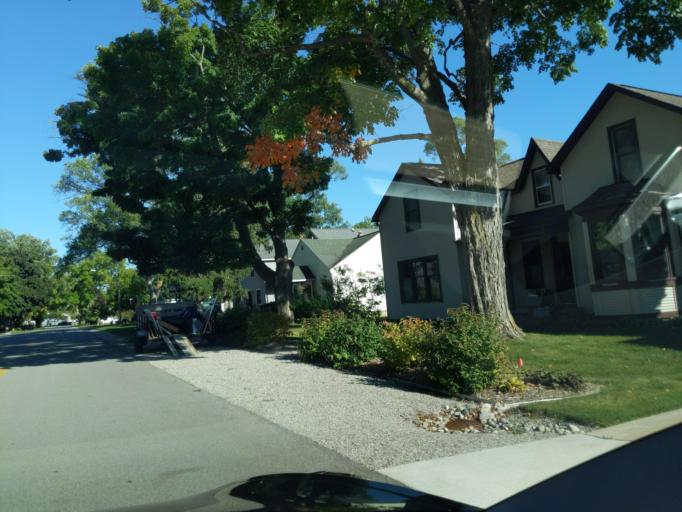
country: US
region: Michigan
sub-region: Antrim County
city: Elk Rapids
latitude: 44.8969
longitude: -85.4149
